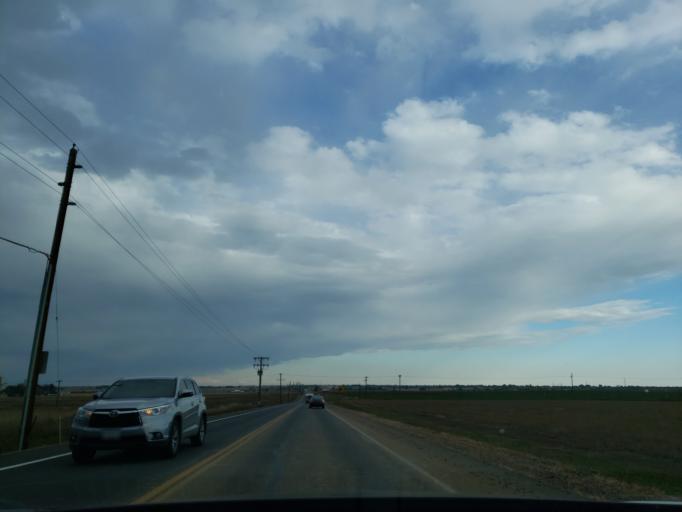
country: US
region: Colorado
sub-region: Larimer County
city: Fort Collins
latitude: 40.6102
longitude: -105.0318
